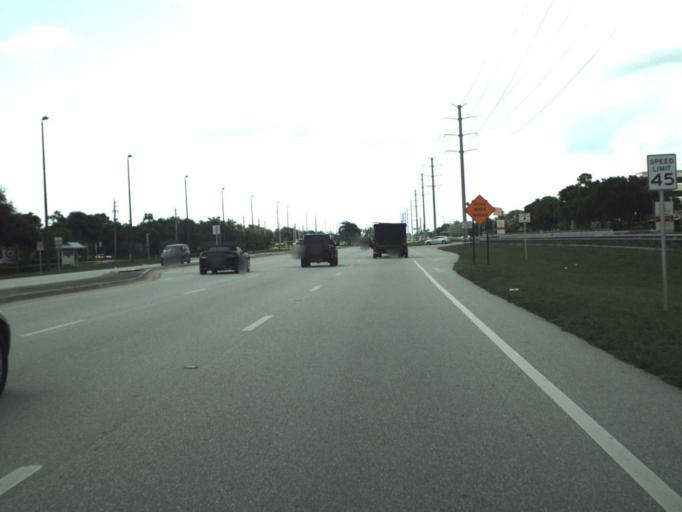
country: US
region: Florida
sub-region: Palm Beach County
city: Boca Pointe
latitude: 26.3530
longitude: -80.2032
